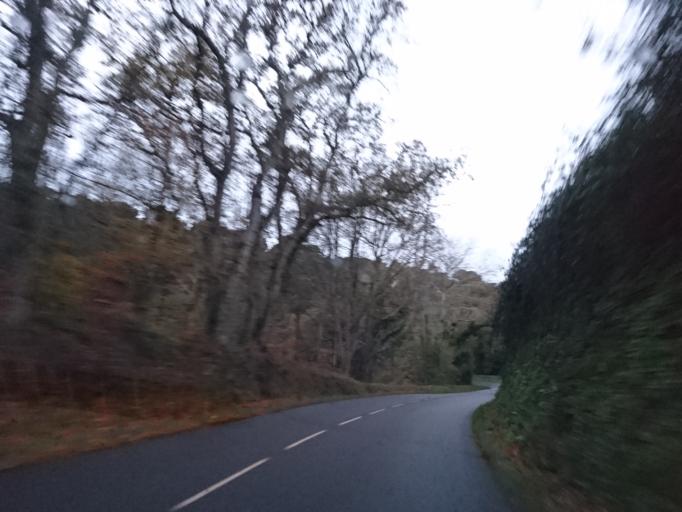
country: FR
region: Brittany
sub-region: Departement du Finistere
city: Le Conquet
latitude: 48.3661
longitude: -4.7459
